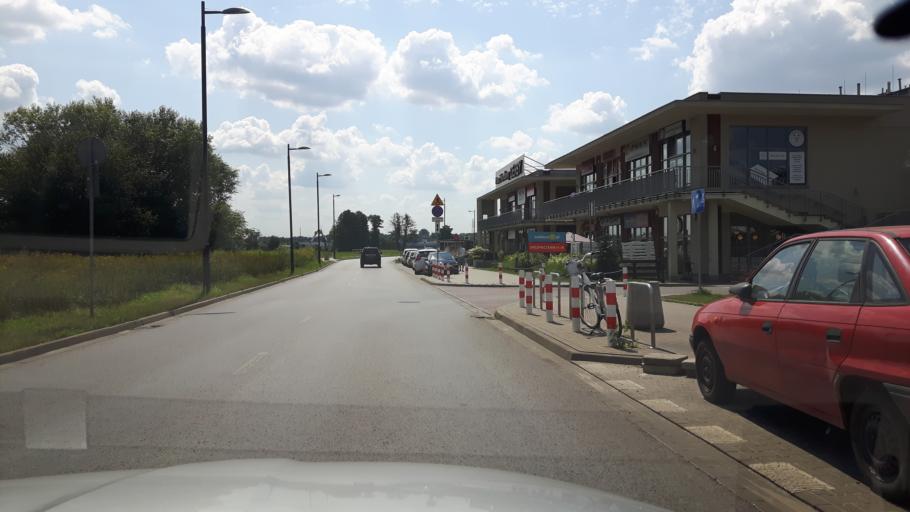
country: PL
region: Masovian Voivodeship
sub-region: Warszawa
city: Targowek
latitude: 52.3143
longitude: 21.0607
